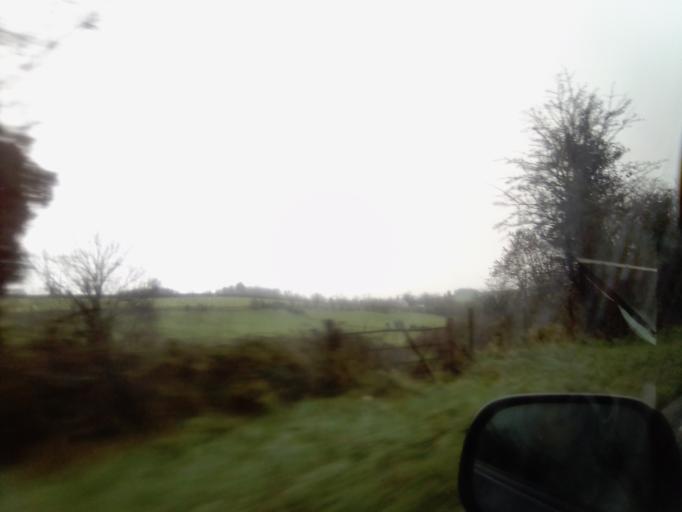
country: GB
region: Northern Ireland
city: Newtownstewart
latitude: 54.7026
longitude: -7.3547
